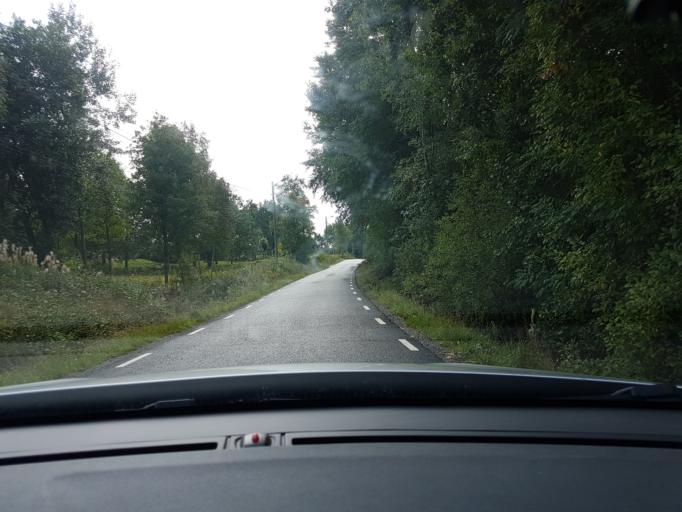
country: SE
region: Vaestra Goetaland
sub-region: Ale Kommun
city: Skepplanda
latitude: 57.8964
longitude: 12.1942
